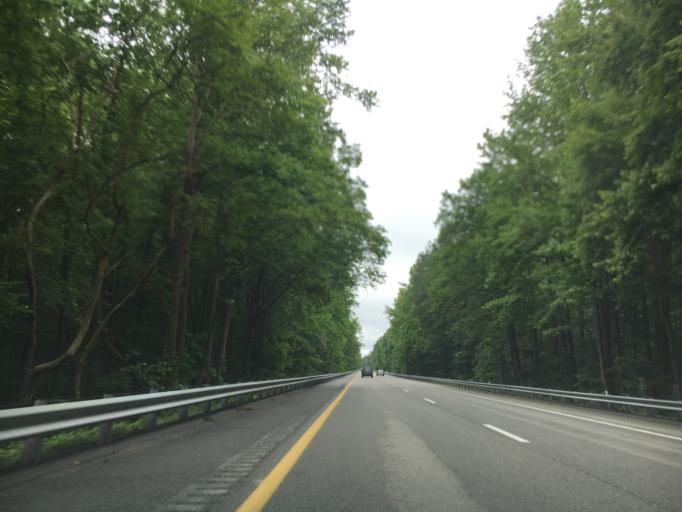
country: US
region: Virginia
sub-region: Brunswick County
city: Lawrenceville
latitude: 36.9120
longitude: -77.7768
